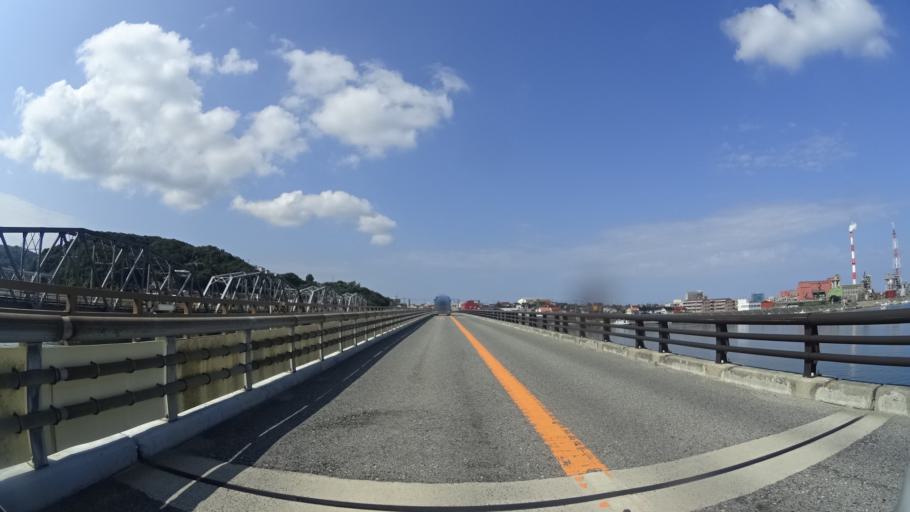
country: JP
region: Shimane
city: Gotsucho
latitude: 35.0155
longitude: 132.2300
